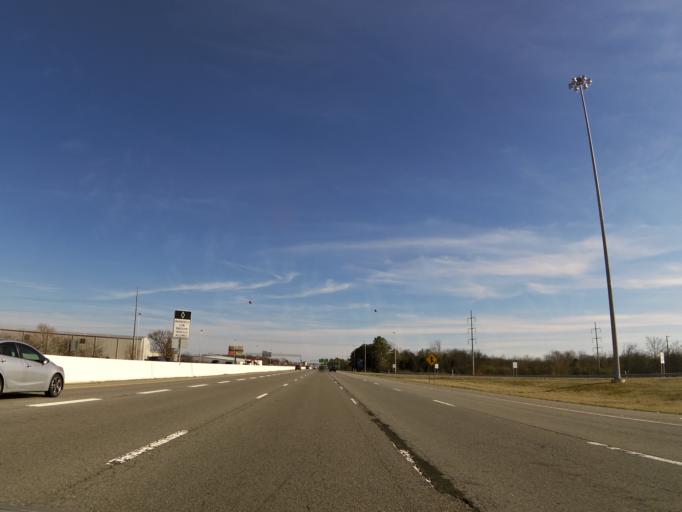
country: US
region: Tennessee
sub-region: Rutherford County
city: Murfreesboro
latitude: 35.8263
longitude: -86.4123
